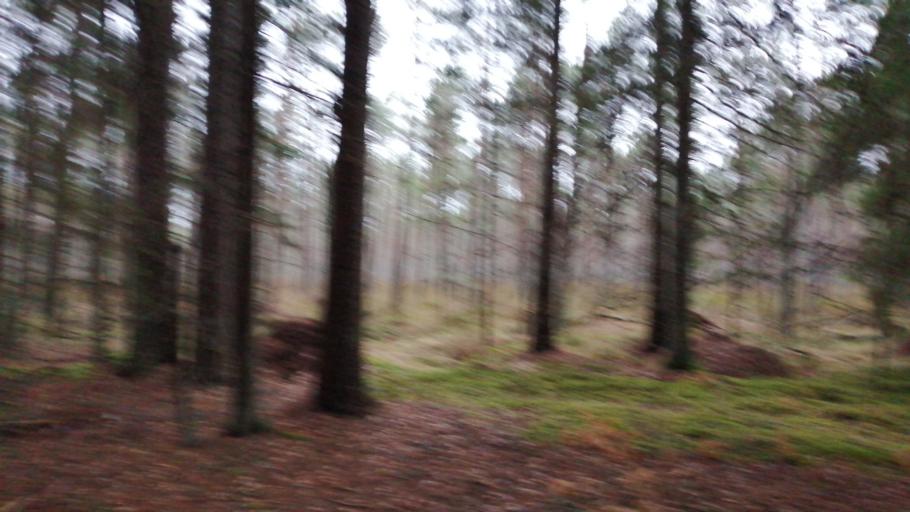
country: EE
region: Polvamaa
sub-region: Polva linn
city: Polva
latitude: 58.1539
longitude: 27.0680
